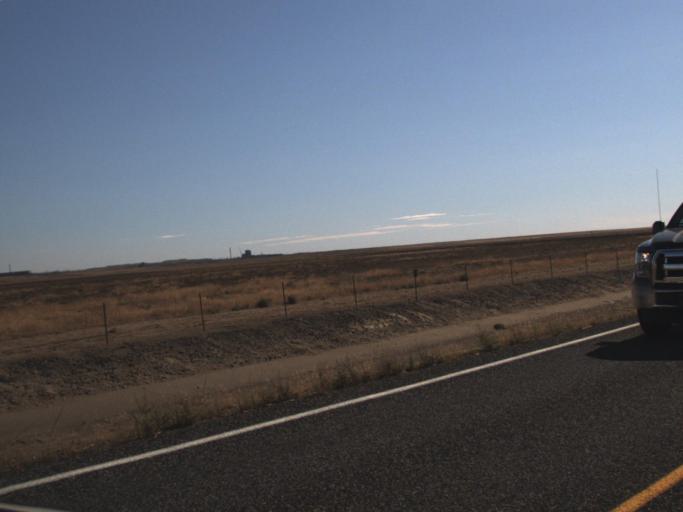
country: US
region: Washington
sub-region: Grant County
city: Desert Aire
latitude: 46.5461
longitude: -119.6900
